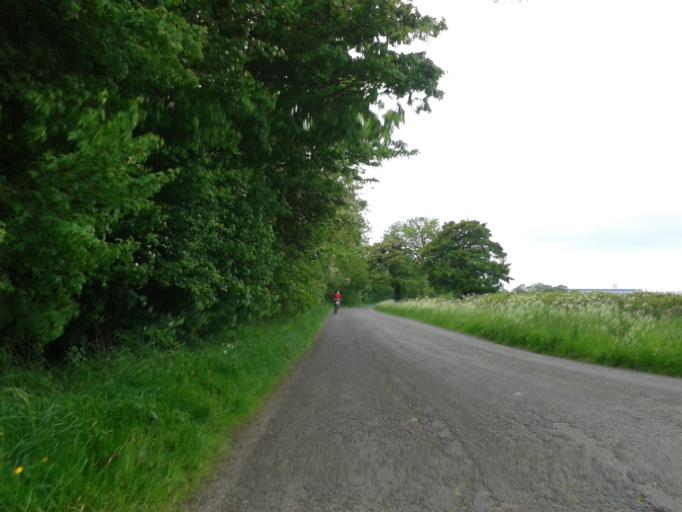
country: GB
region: England
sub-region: Northamptonshire
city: Corby
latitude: 52.5211
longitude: -0.6317
